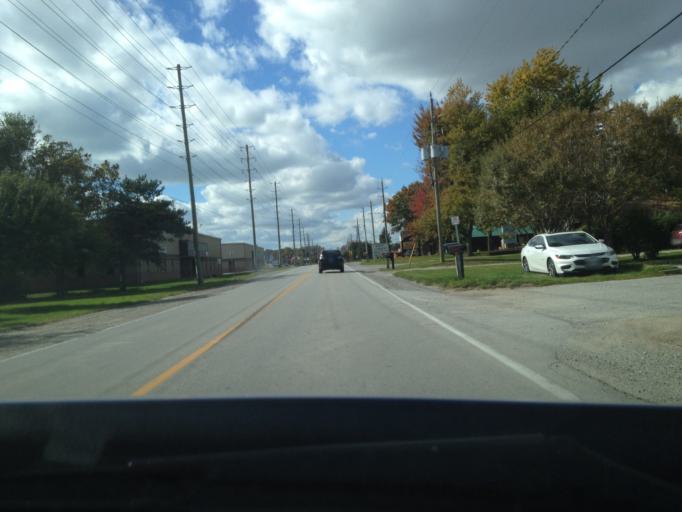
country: CA
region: Ontario
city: Amherstburg
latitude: 42.0335
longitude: -82.5893
